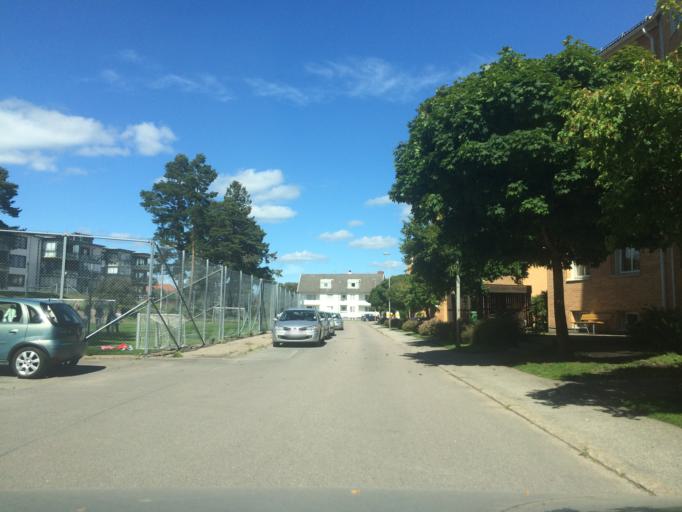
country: SE
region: Vaestra Goetaland
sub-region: Trollhattan
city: Trollhattan
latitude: 58.2858
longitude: 12.3105
